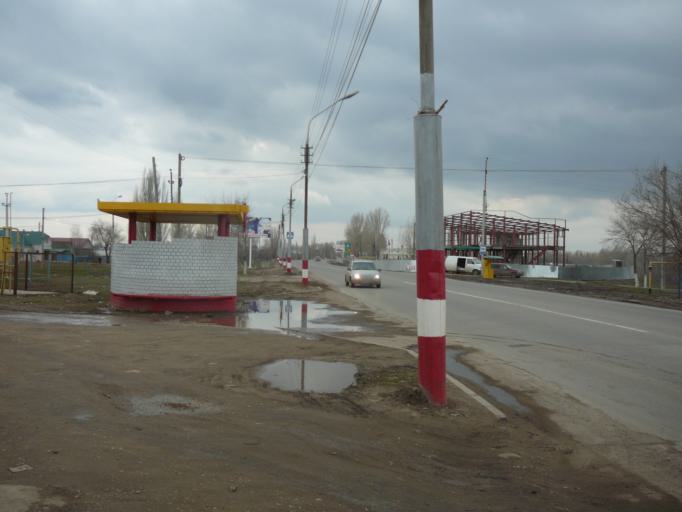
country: RU
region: Saratov
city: Engel's
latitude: 51.4661
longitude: 46.0955
